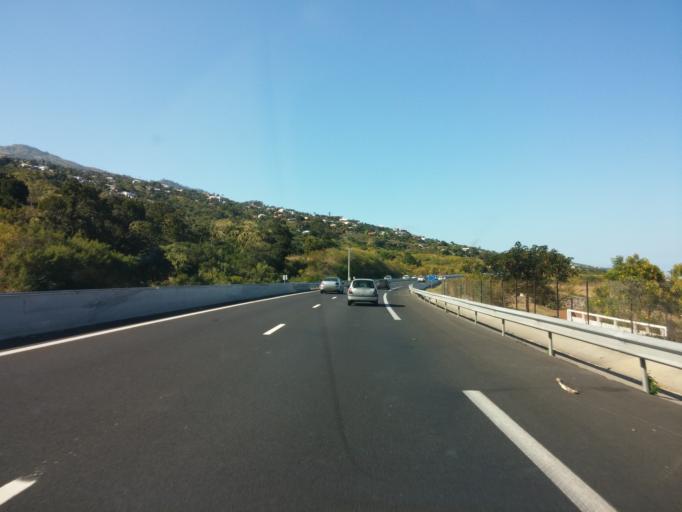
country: RE
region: Reunion
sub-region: Reunion
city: Saint-Leu
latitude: -21.1609
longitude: 55.2967
